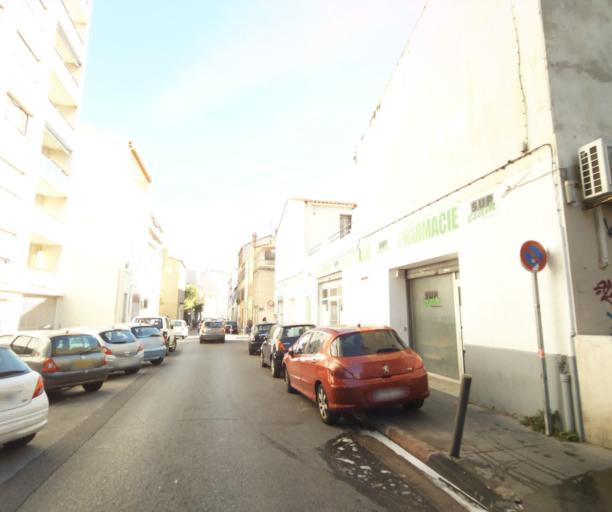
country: FR
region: Provence-Alpes-Cote d'Azur
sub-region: Departement des Bouches-du-Rhone
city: Marseille 05
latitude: 43.2884
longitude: 5.3960
